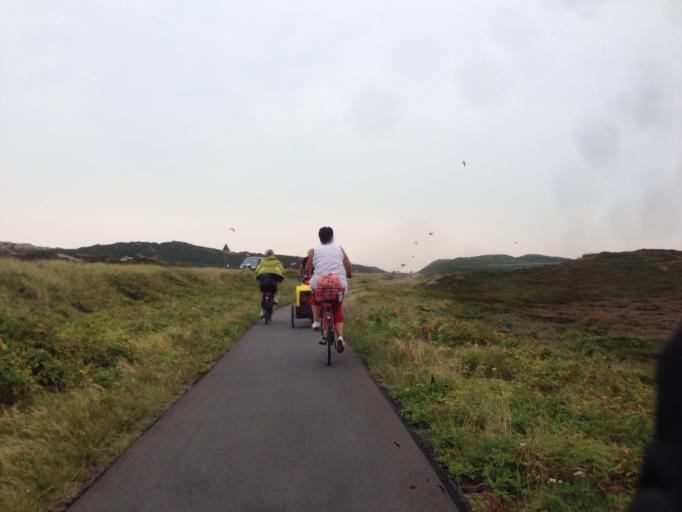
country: DE
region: Schleswig-Holstein
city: Westerland
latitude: 54.8001
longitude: 8.2880
